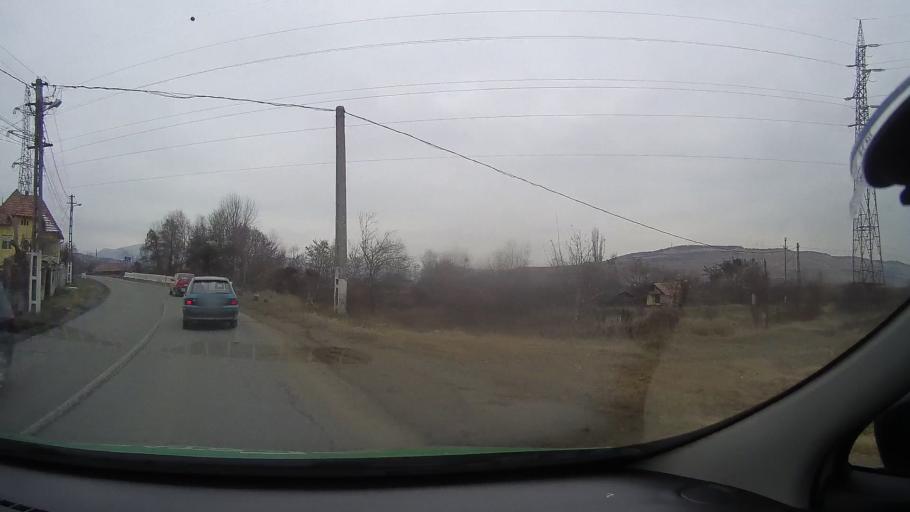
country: RO
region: Alba
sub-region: Comuna Ighiu
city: Sard
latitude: 46.1196
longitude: 23.5346
